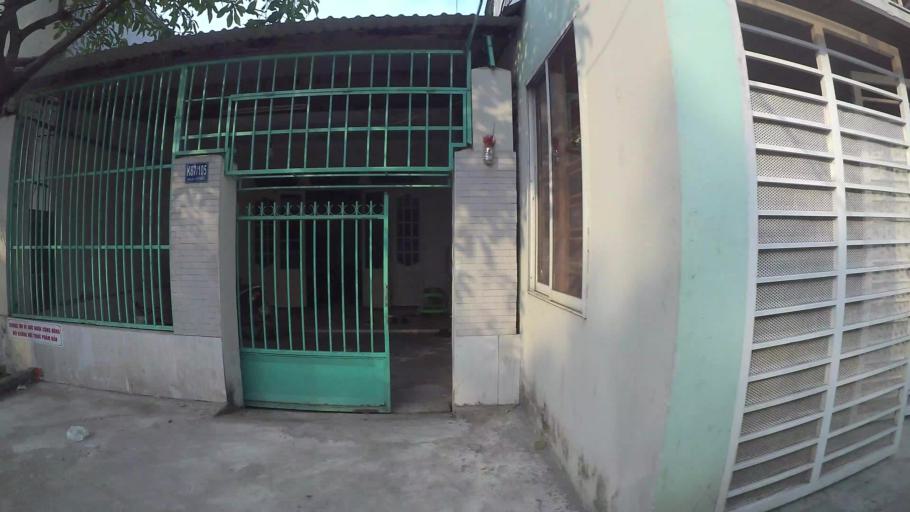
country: VN
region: Da Nang
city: Lien Chieu
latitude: 16.0501
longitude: 108.1576
